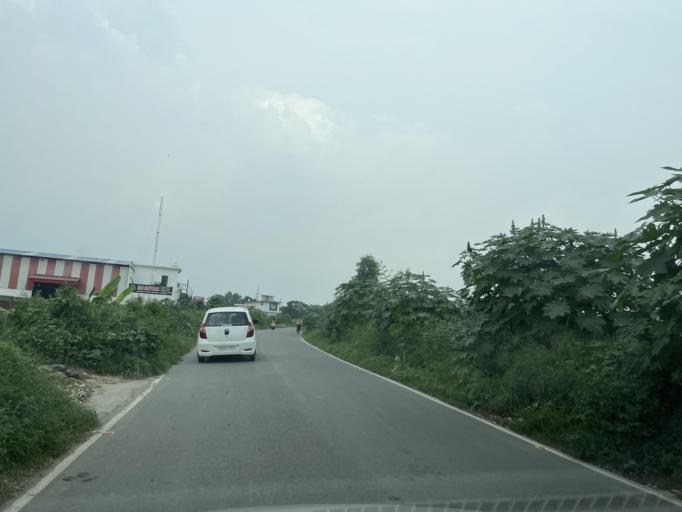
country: IN
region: Uttarakhand
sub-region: Naini Tal
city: Haldwani
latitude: 29.1877
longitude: 79.4776
